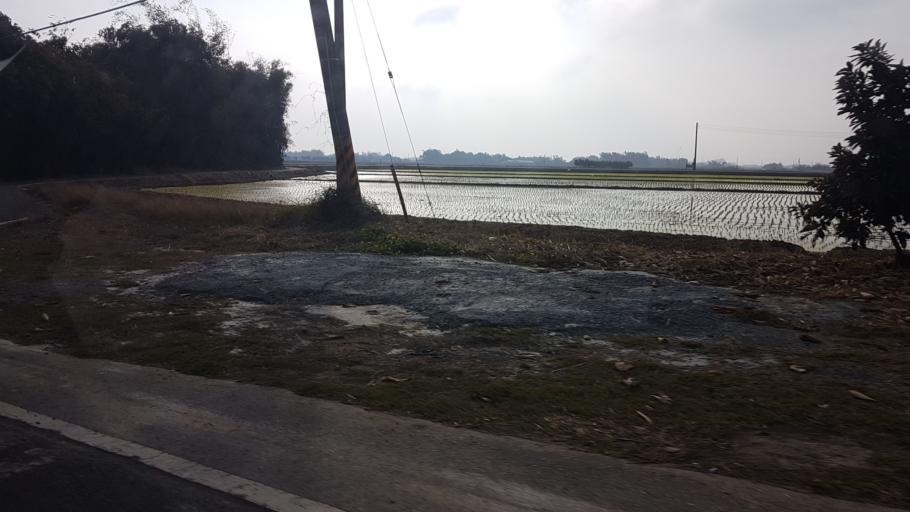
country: TW
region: Taiwan
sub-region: Chiayi
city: Jiayi Shi
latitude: 23.4022
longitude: 120.4287
